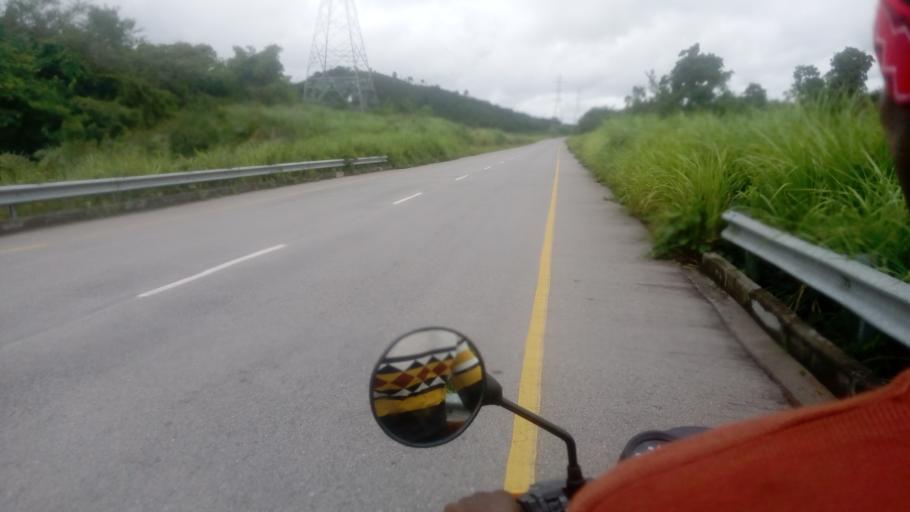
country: SL
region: Northern Province
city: Masaka
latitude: 8.6492
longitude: -11.7667
